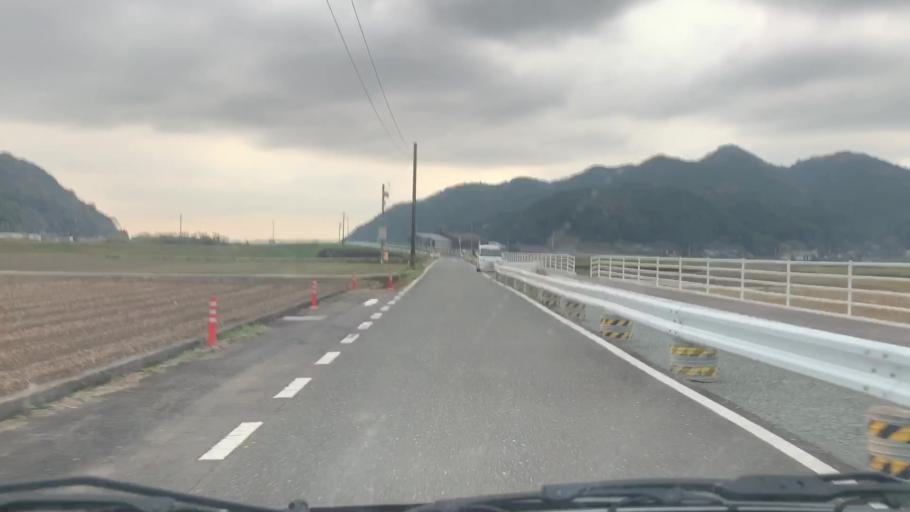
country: JP
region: Saga Prefecture
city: Ureshinomachi-shimojuku
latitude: 33.1266
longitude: 130.0335
